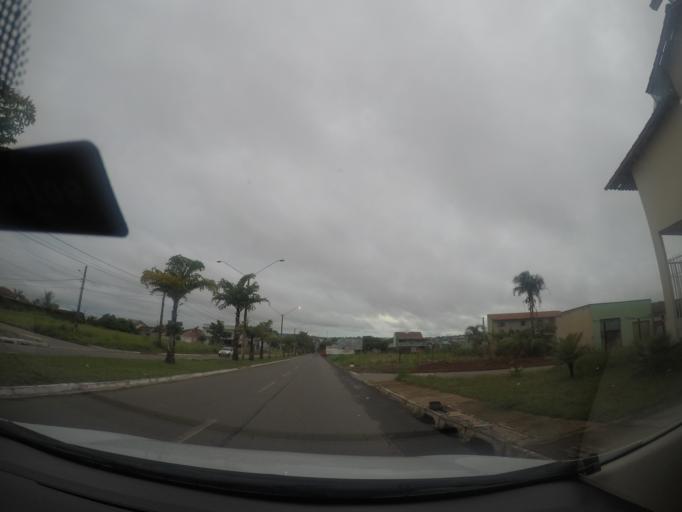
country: BR
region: Goias
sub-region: Goiania
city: Goiania
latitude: -16.7543
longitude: -49.3221
